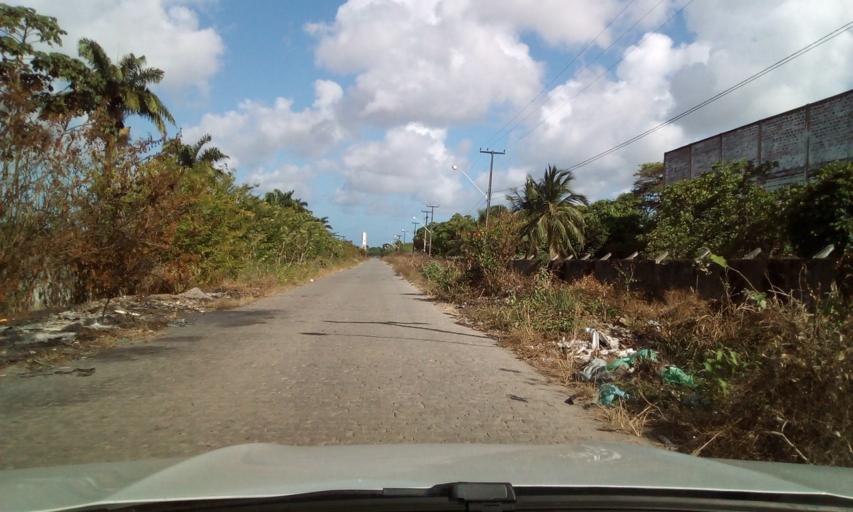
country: BR
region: Paraiba
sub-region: Bayeux
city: Bayeux
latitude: -7.1815
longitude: -34.9147
